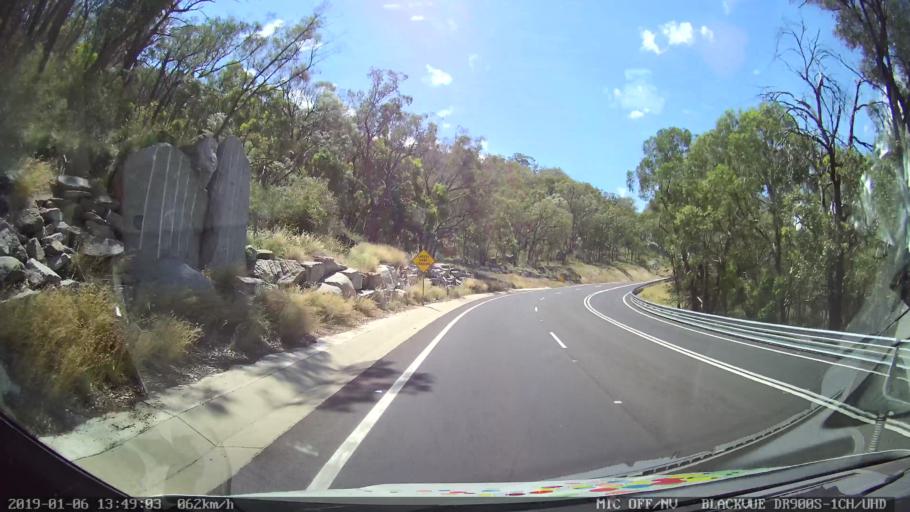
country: AU
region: New South Wales
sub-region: Tamworth Municipality
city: Kootingal
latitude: -30.9456
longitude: 151.1085
